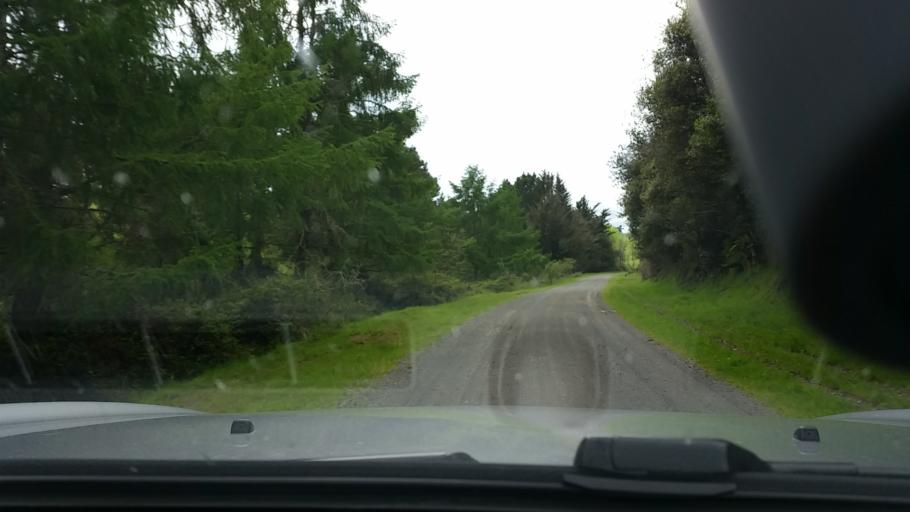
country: NZ
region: Waikato
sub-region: Taupo District
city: Taupo
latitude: -38.4606
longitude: 176.2408
